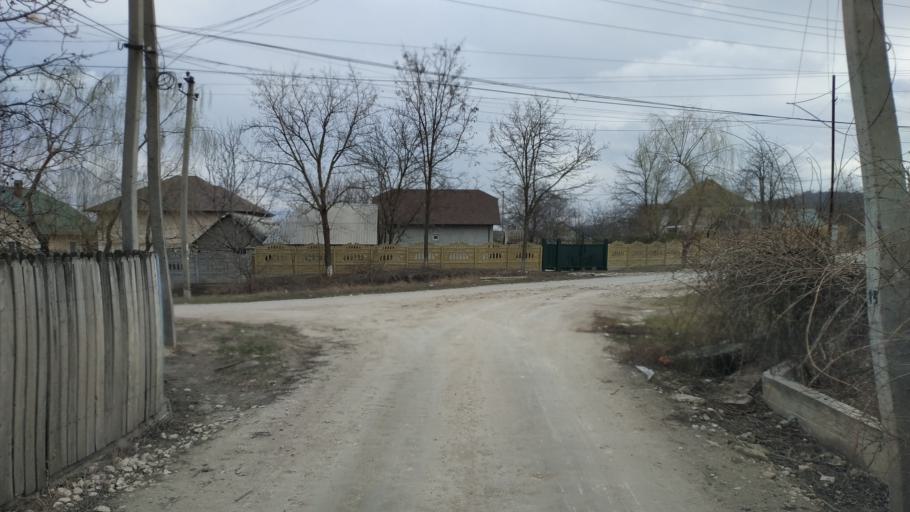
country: MD
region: Laloveni
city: Ialoveni
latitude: 46.8572
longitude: 28.7861
